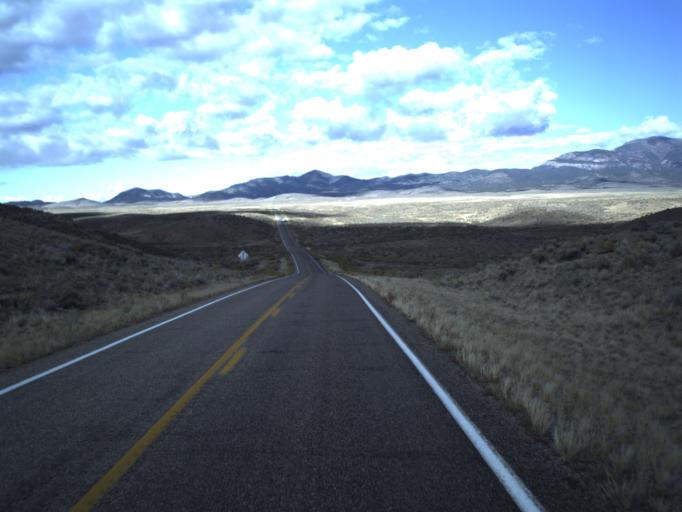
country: US
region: Utah
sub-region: Beaver County
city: Milford
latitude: 38.4381
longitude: -113.1486
